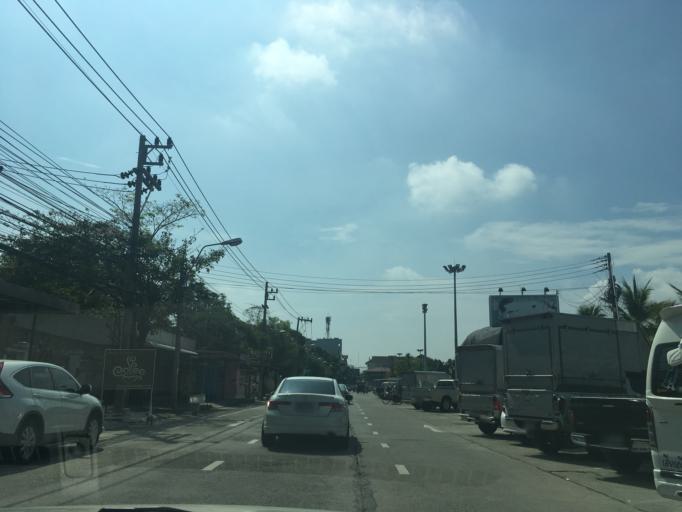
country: TH
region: Chon Buri
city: Chon Buri
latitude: 13.3636
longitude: 100.9827
